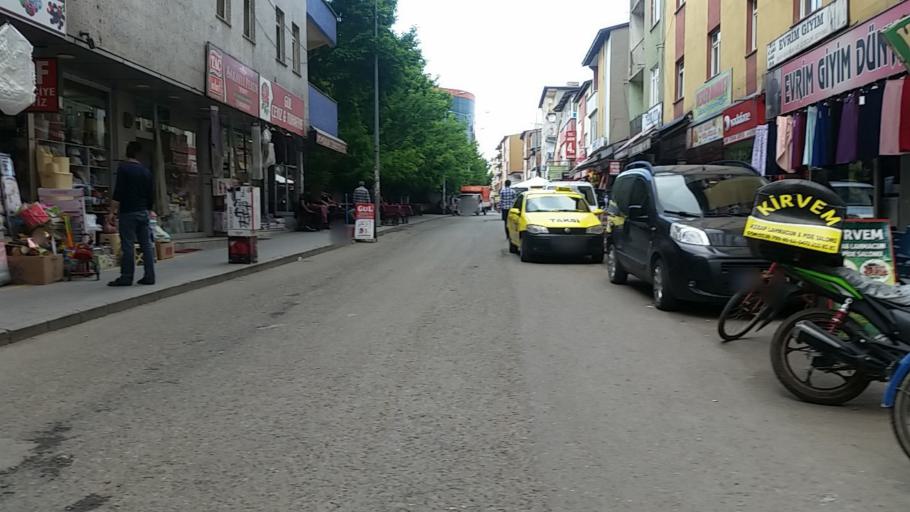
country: TR
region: Agri
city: Agri
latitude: 39.7231
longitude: 43.0536
